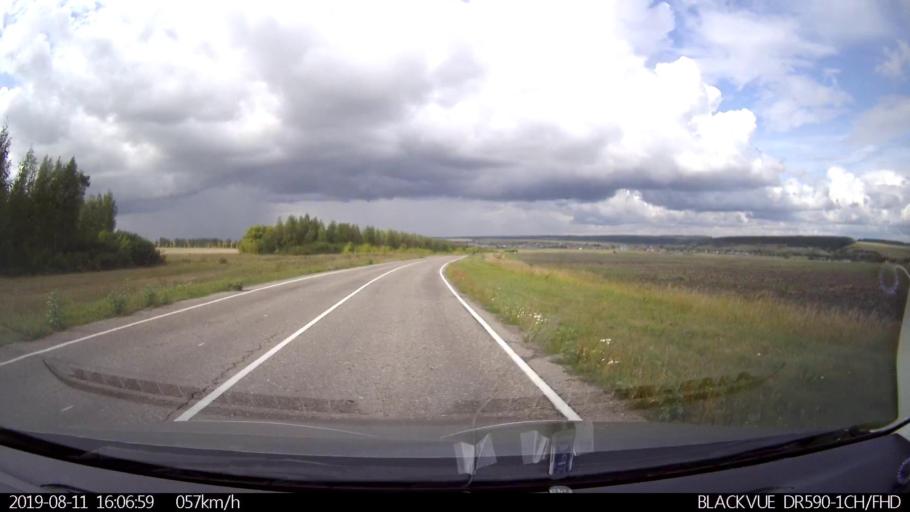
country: RU
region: Ulyanovsk
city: Ignatovka
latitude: 53.9735
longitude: 47.6447
